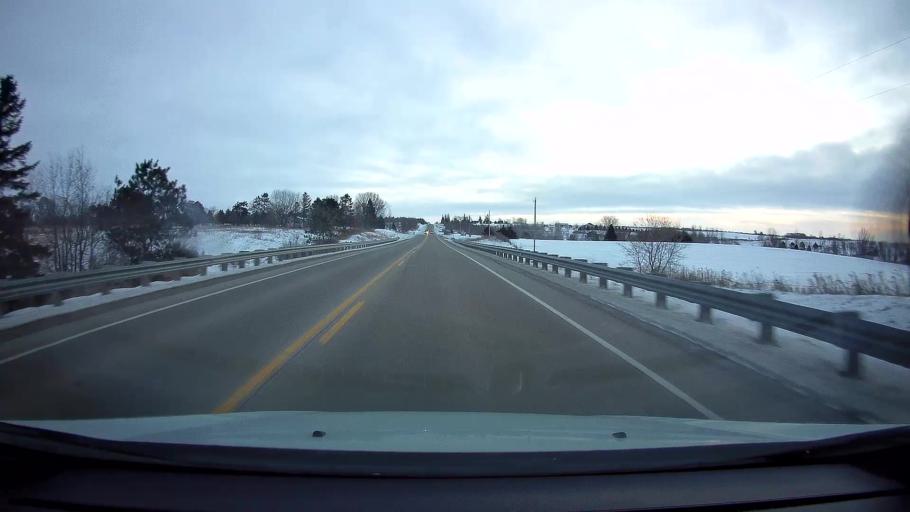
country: US
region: Wisconsin
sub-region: Saint Croix County
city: New Richmond
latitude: 45.1371
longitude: -92.5102
